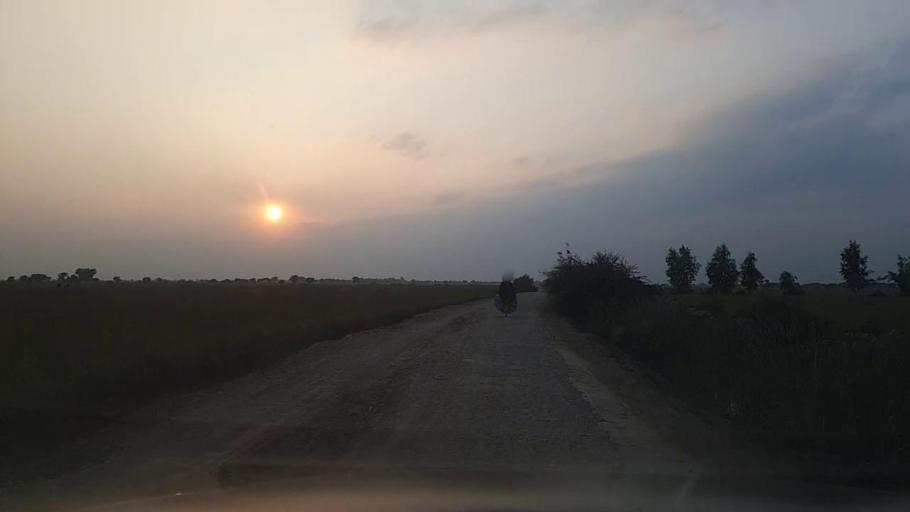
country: PK
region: Sindh
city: Jati
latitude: 24.5297
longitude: 68.4004
